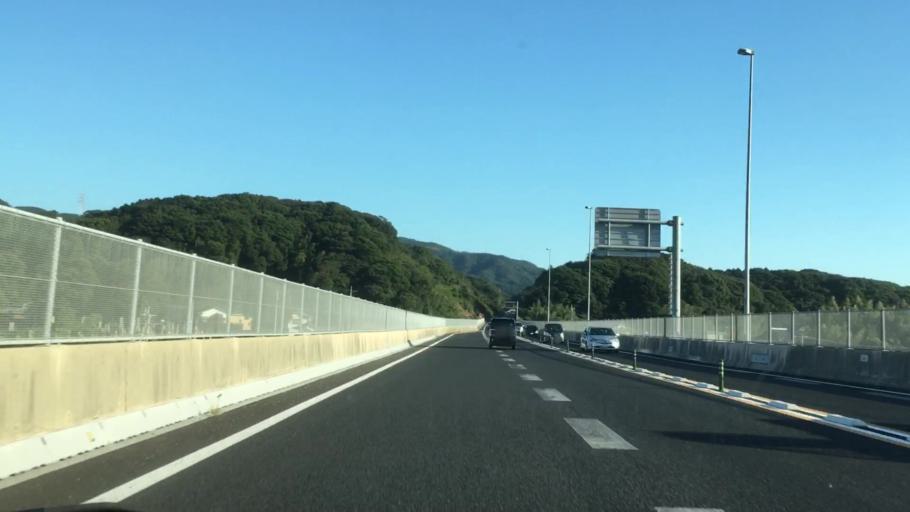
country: JP
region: Nagasaki
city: Sasebo
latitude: 33.2010
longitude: 129.6738
